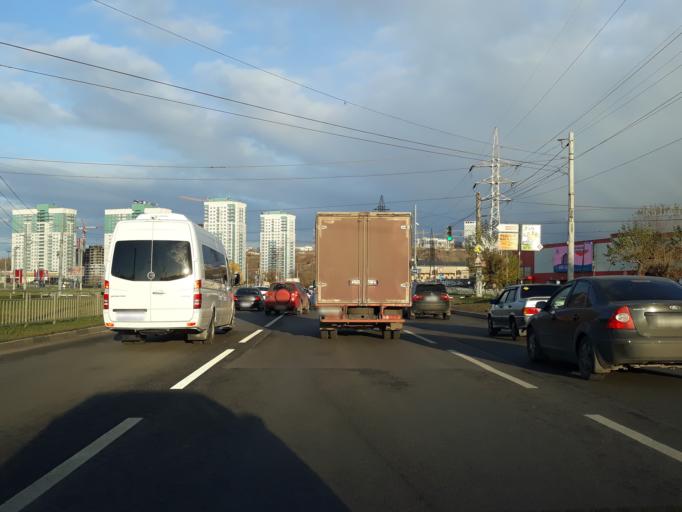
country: RU
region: Nizjnij Novgorod
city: Nizhniy Novgorod
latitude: 56.2973
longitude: 43.9427
